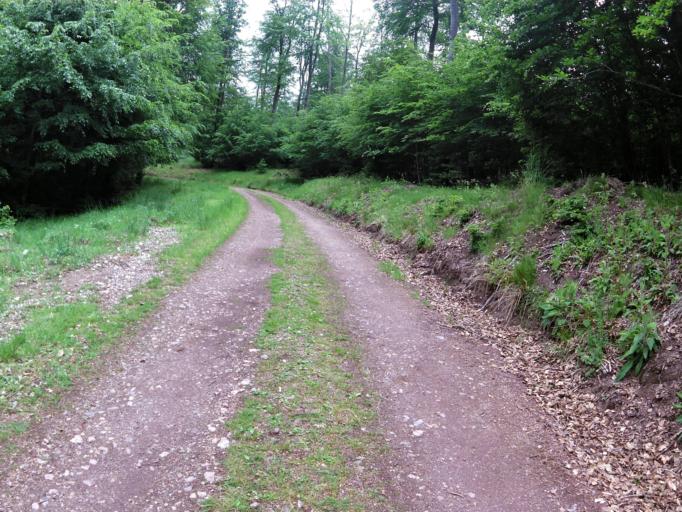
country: DE
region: Thuringia
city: Eisenach
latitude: 50.9455
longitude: 10.3168
